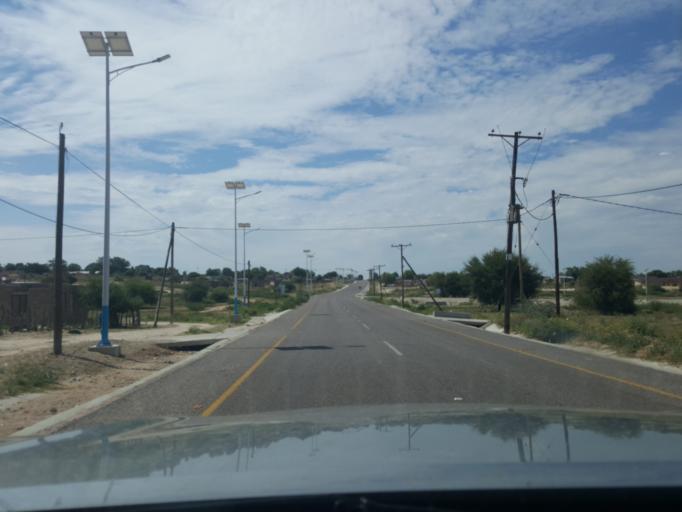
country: BW
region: Kweneng
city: Letlhakeng
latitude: -24.0916
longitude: 25.0301
